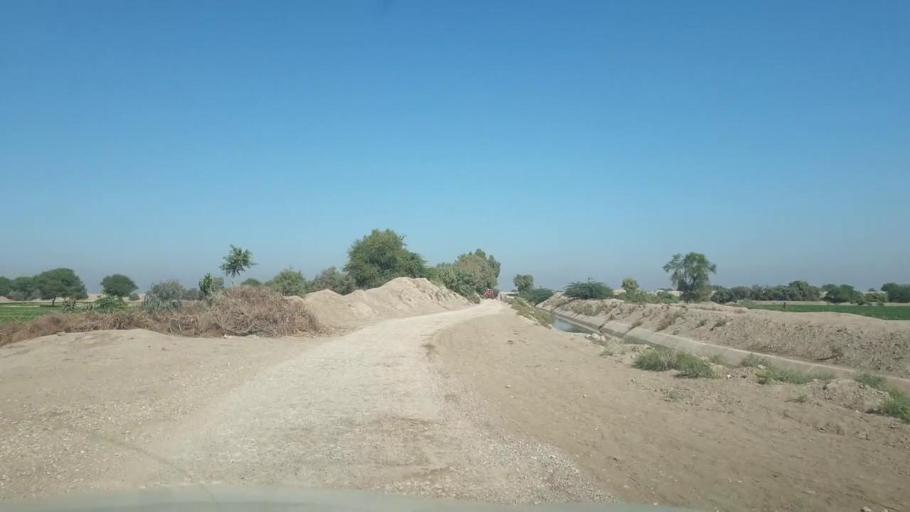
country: PK
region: Sindh
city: Bhan
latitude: 26.5595
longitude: 67.6299
